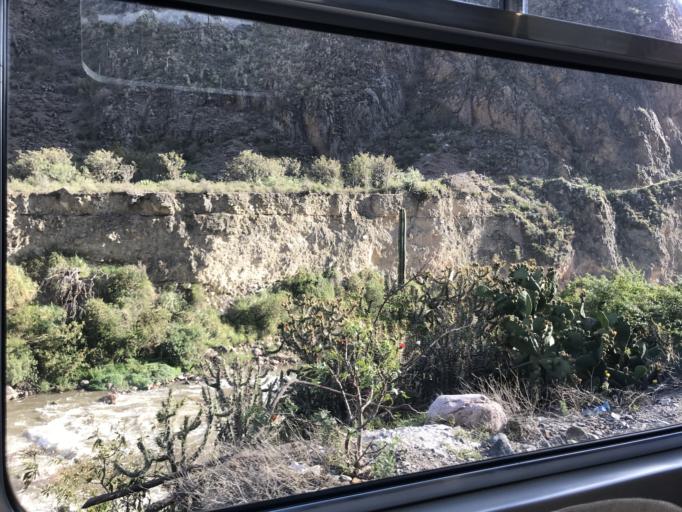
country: PE
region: Cusco
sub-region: Provincia de Urubamba
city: Ollantaytambo
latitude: -13.2148
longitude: -72.3817
